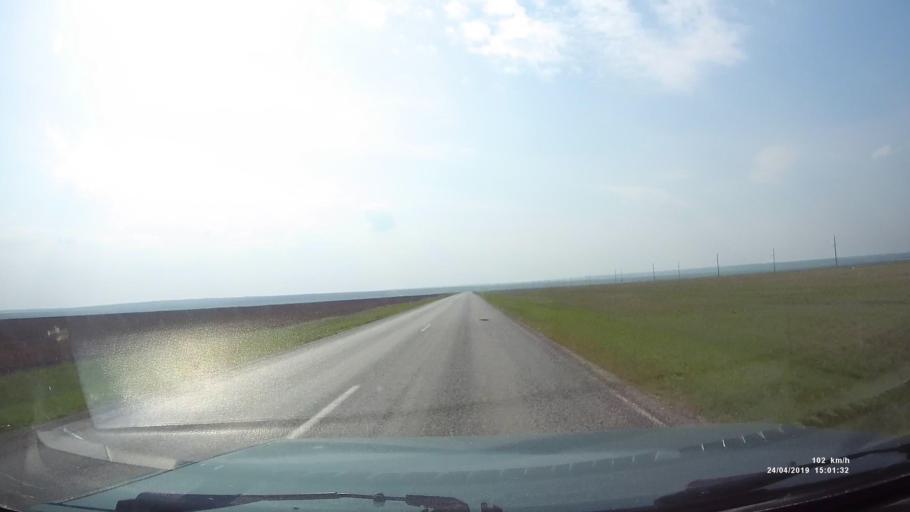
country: RU
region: Rostov
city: Remontnoye
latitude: 46.5661
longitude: 43.5317
